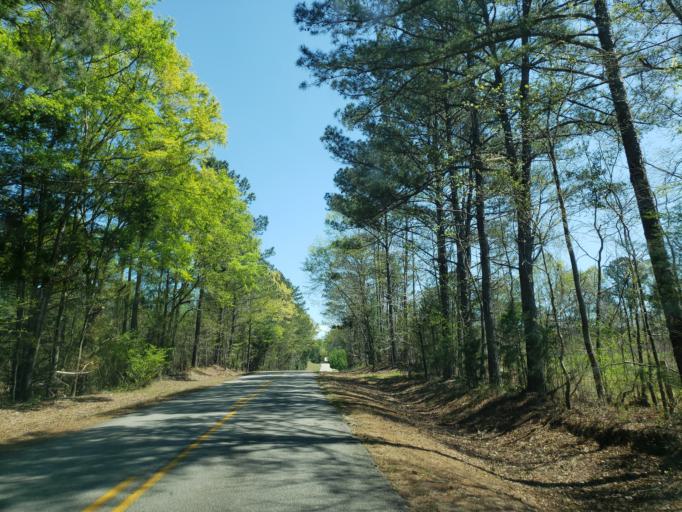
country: US
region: Alabama
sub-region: Tallapoosa County
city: Camp Hill
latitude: 32.6869
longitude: -85.6722
